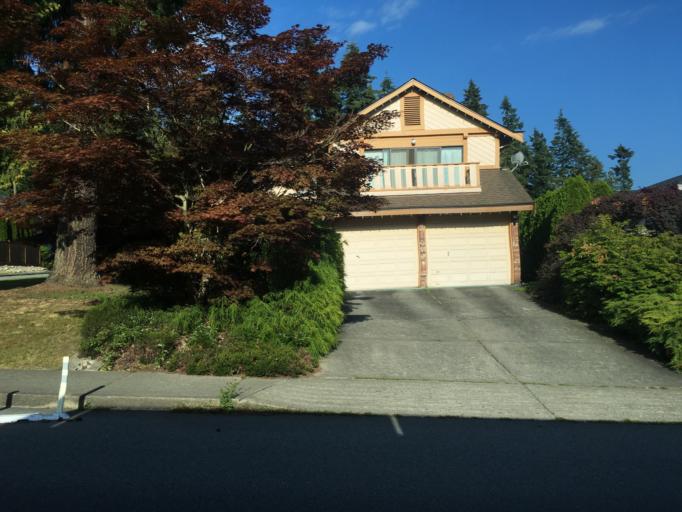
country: CA
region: British Columbia
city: Port Moody
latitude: 49.2452
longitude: -122.8244
